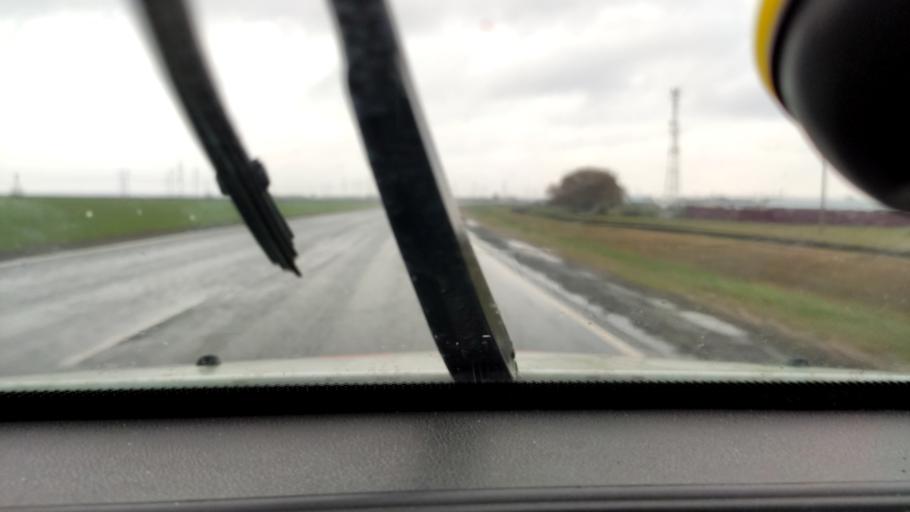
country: RU
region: Samara
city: Povolzhskiy
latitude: 53.6375
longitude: 49.6590
